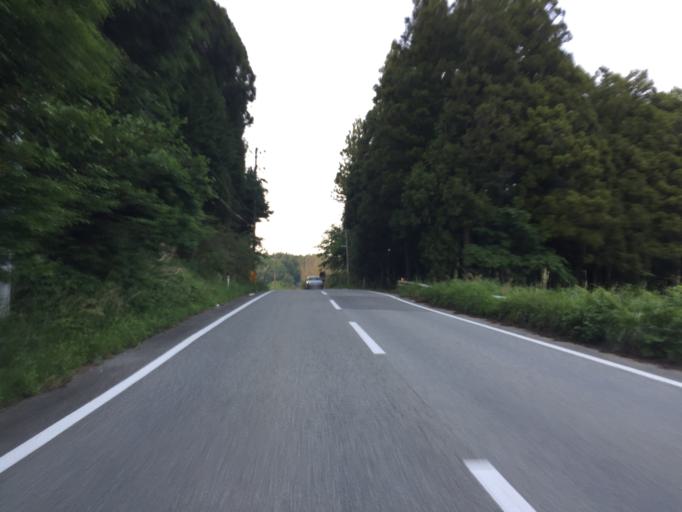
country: JP
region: Fukushima
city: Namie
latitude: 37.2671
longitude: 140.9747
